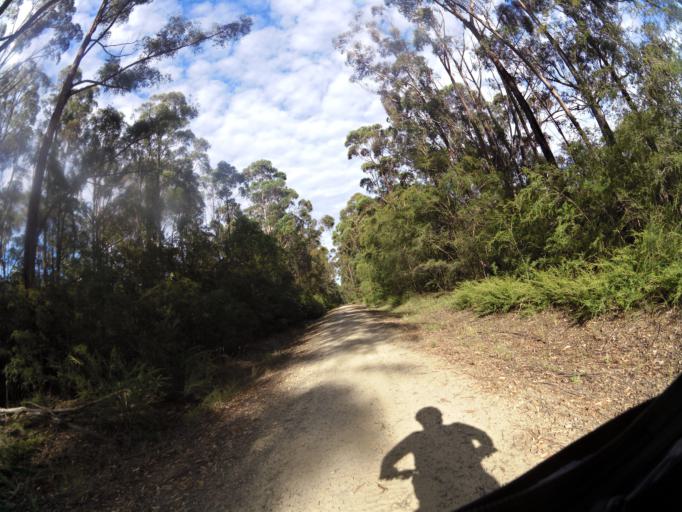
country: AU
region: Victoria
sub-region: East Gippsland
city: Lakes Entrance
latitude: -37.7448
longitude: 148.3799
